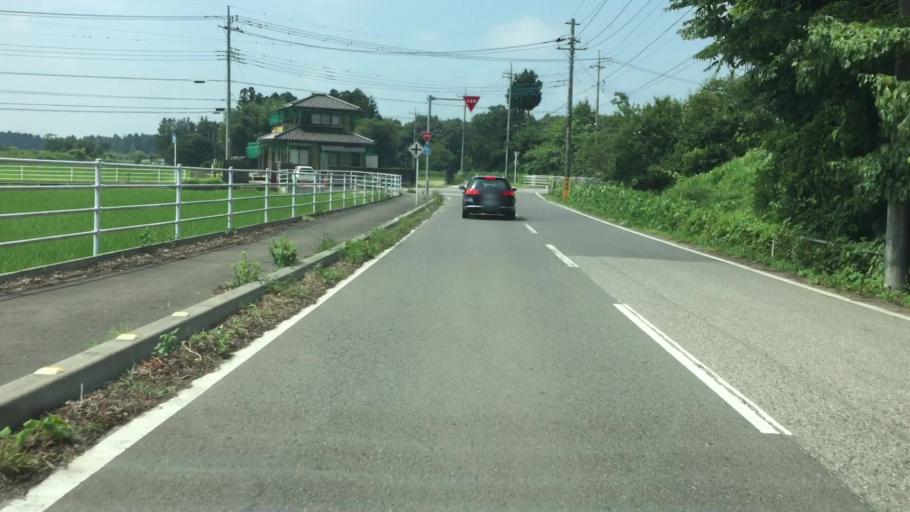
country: JP
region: Tochigi
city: Kuroiso
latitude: 36.9730
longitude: 139.9685
